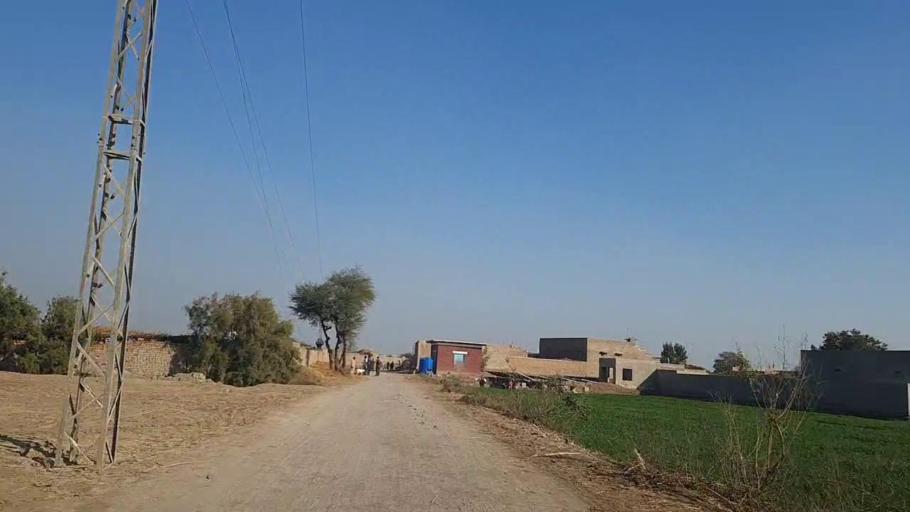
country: PK
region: Sindh
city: Daur
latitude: 26.3179
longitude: 68.1743
